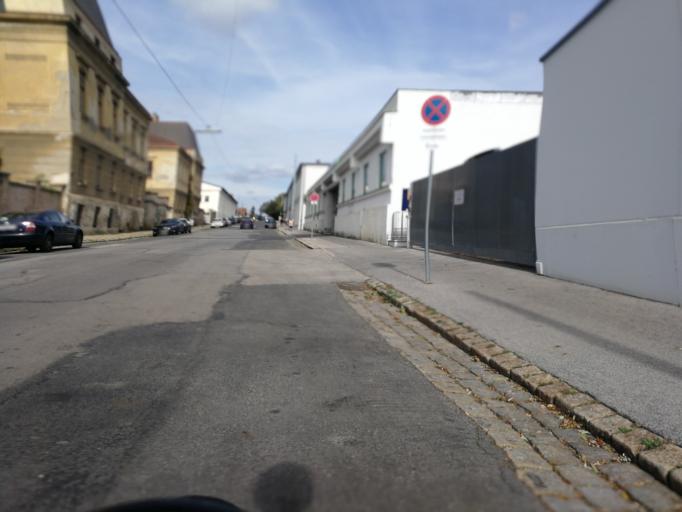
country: AT
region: Vienna
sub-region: Wien Stadt
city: Vienna
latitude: 48.2029
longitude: 16.3020
